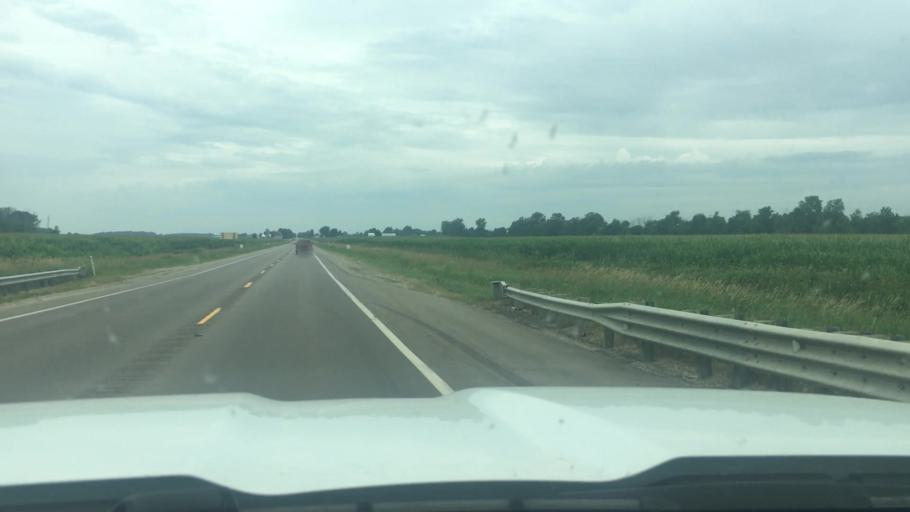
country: US
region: Michigan
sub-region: Clinton County
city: Fowler
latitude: 43.0016
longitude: -84.6615
